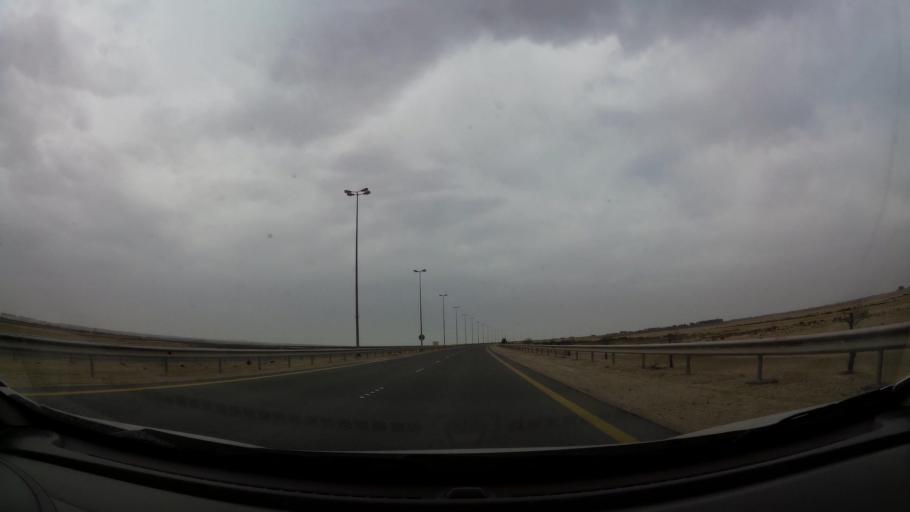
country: BH
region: Central Governorate
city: Dar Kulayb
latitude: 26.0057
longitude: 50.4847
